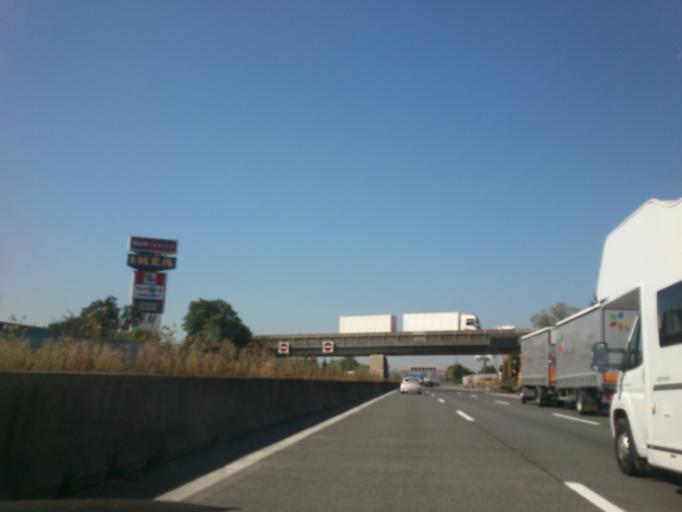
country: AT
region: Upper Austria
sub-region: Politischer Bezirk Linz-Land
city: Traun
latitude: 48.1987
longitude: 14.2497
